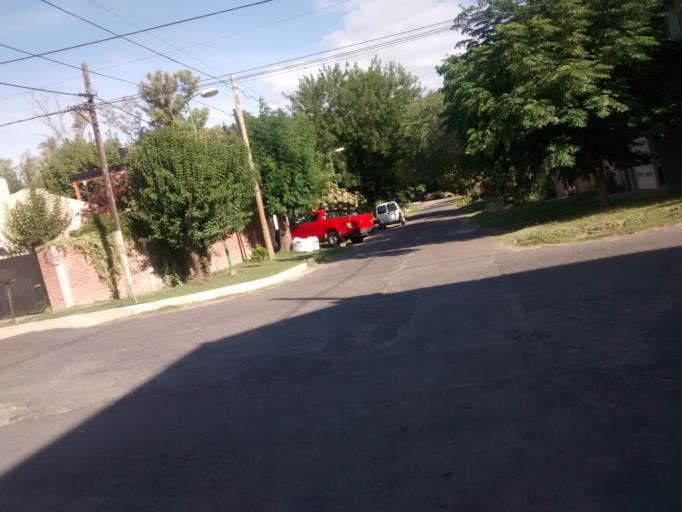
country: AR
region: Buenos Aires
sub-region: Partido de La Plata
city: La Plata
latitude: -34.8580
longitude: -58.0752
